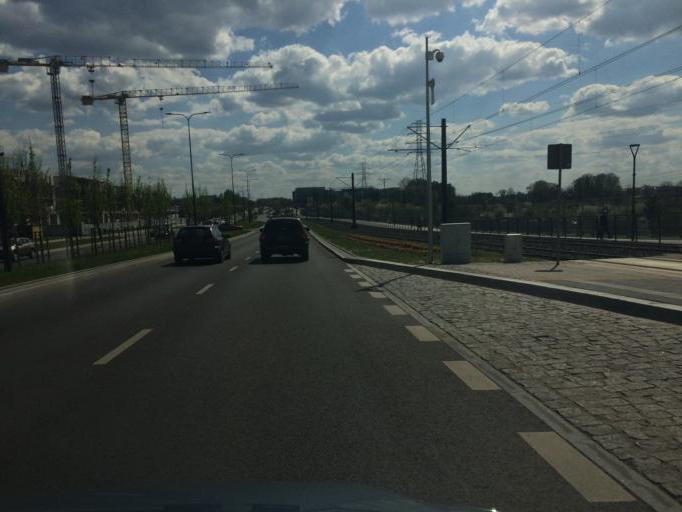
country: PL
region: Warmian-Masurian Voivodeship
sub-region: Powiat olsztynski
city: Olsztyn
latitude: 53.7616
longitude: 20.4868
